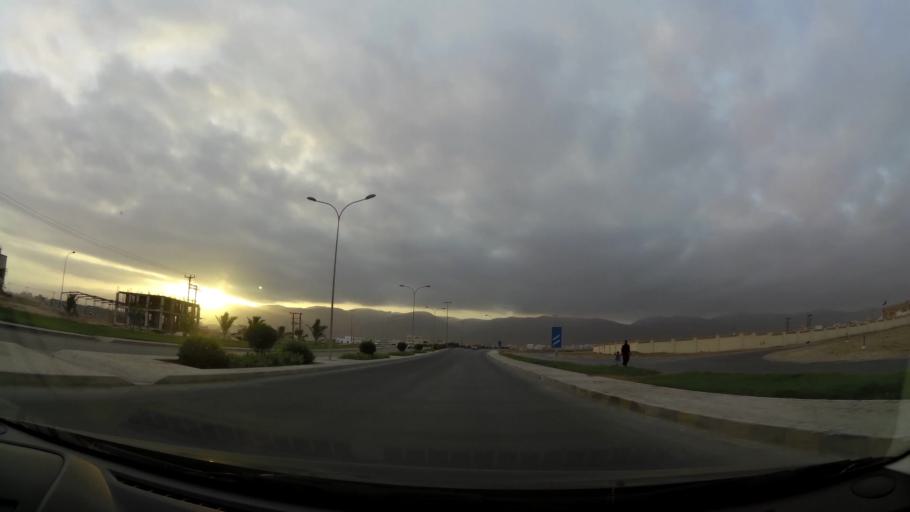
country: OM
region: Zufar
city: Salalah
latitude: 17.0296
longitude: 54.0306
